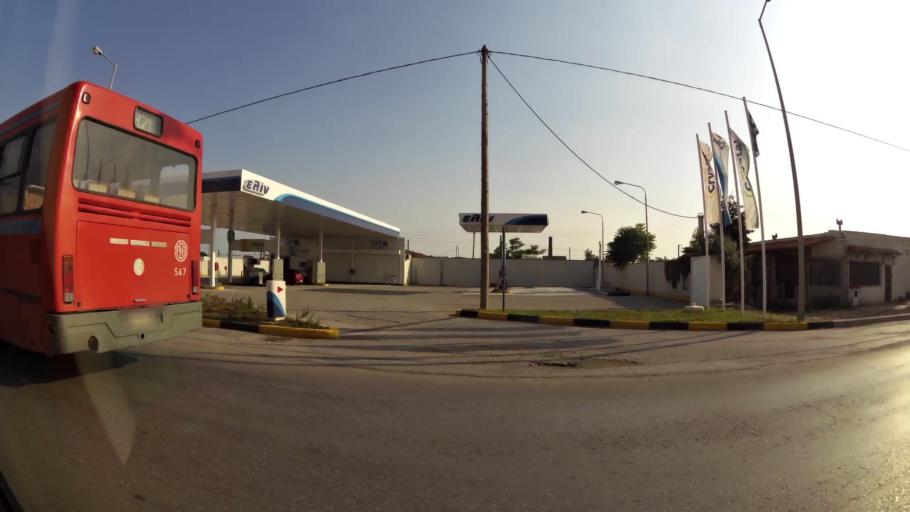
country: GR
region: Central Macedonia
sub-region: Nomos Thessalonikis
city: Diavata
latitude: 40.6760
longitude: 22.8748
